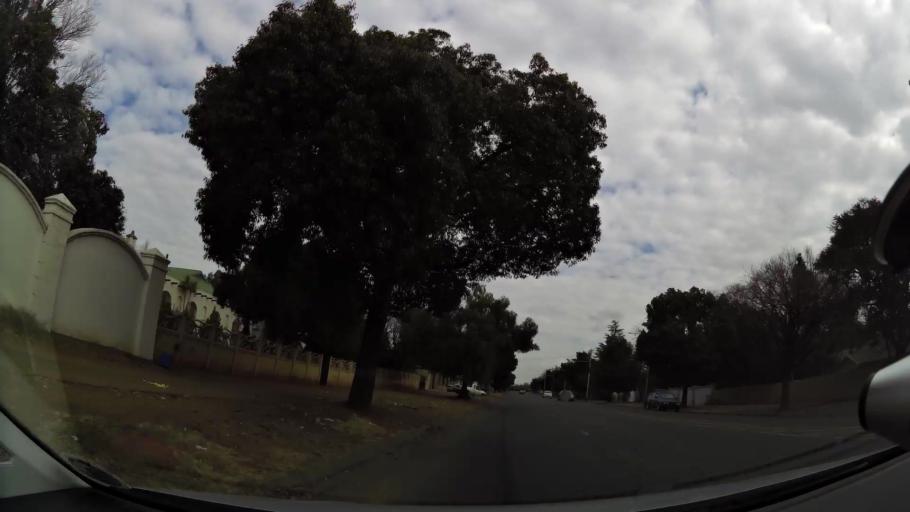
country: ZA
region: Orange Free State
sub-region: Mangaung Metropolitan Municipality
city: Bloemfontein
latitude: -29.0955
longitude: 26.2260
